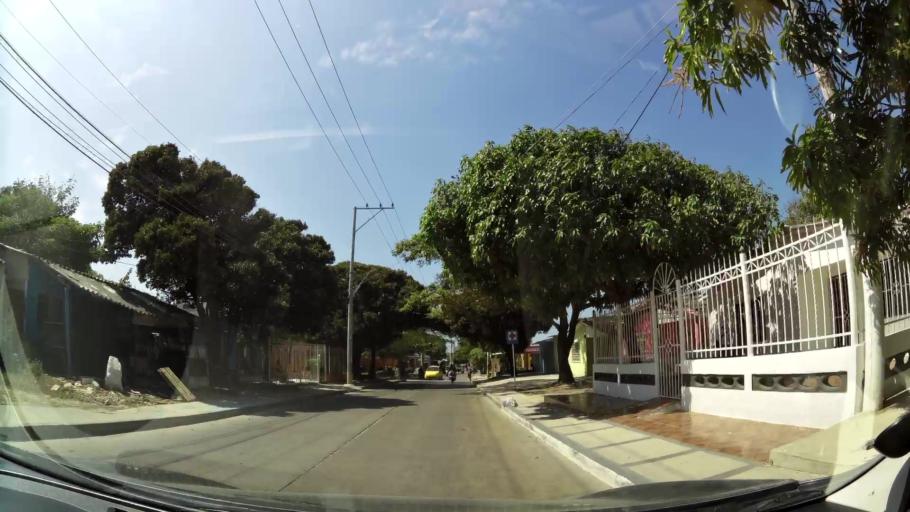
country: CO
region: Atlantico
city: Barranquilla
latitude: 10.9637
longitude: -74.8197
